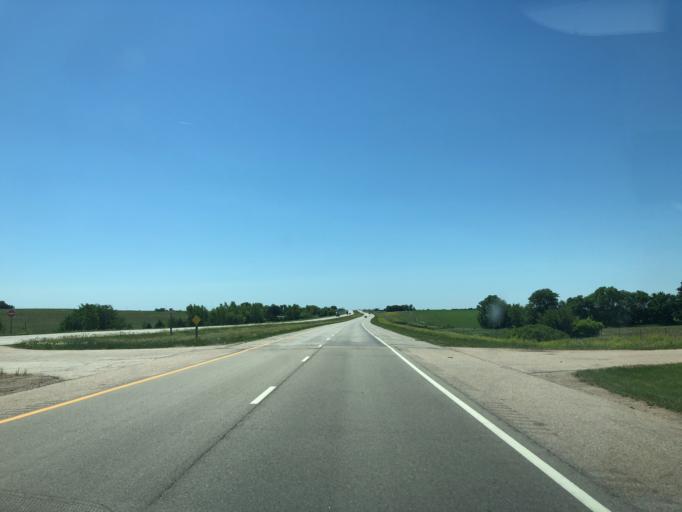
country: US
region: Kansas
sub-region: Republic County
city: Belleville
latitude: 39.9520
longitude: -97.6138
